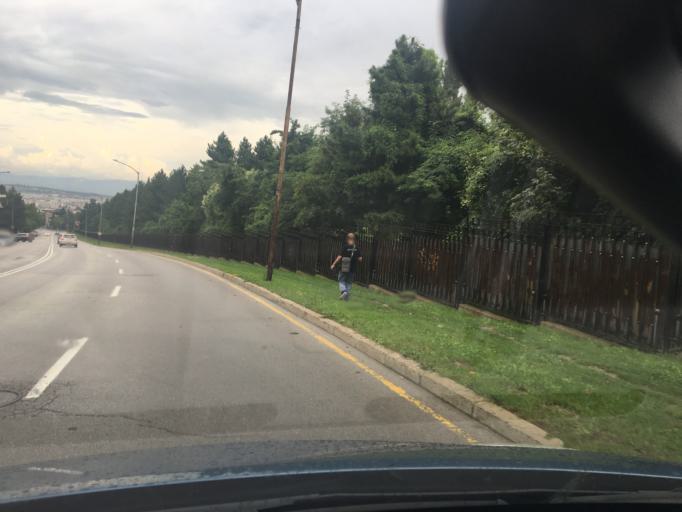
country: BG
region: Sofia-Capital
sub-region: Stolichna Obshtina
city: Sofia
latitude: 42.6512
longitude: 23.2663
